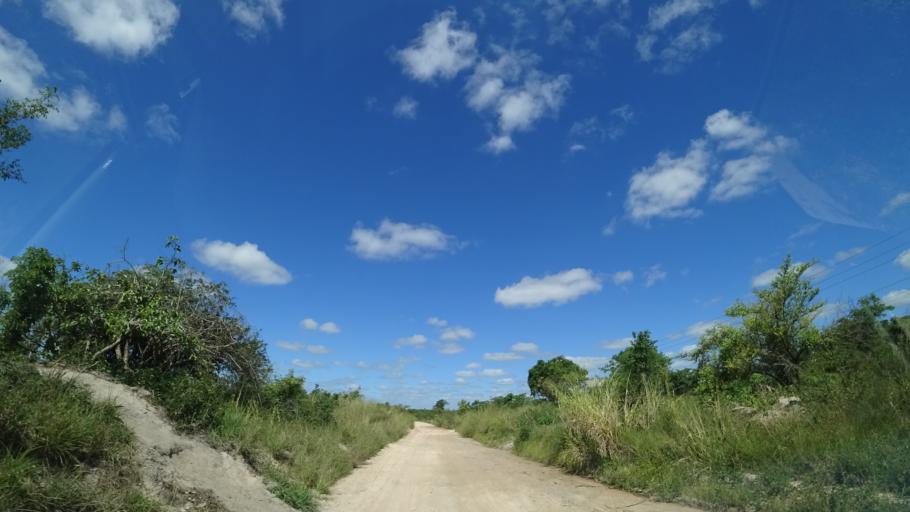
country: MZ
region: Sofala
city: Dondo
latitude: -19.2965
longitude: 34.6906
